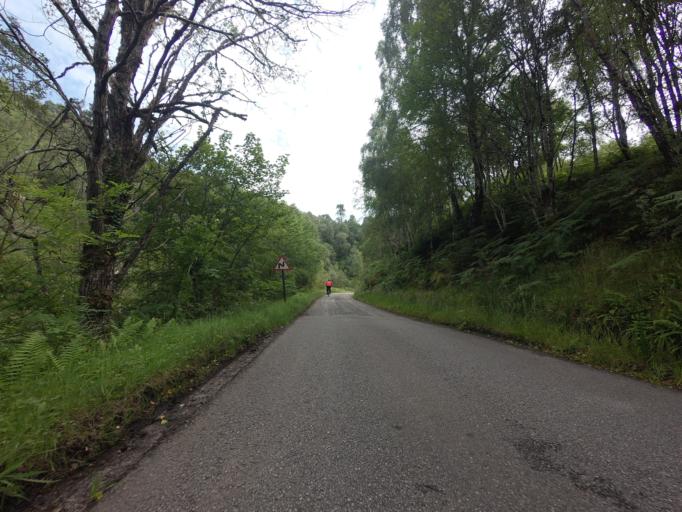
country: GB
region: Scotland
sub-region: Highland
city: Evanton
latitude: 57.9496
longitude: -4.4035
